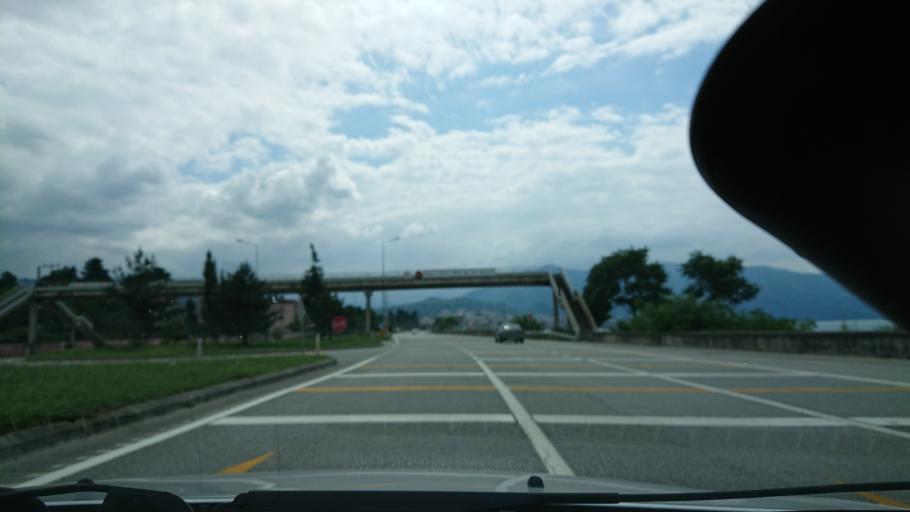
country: TR
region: Trabzon
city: Espiye
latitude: 40.9588
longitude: 38.7309
